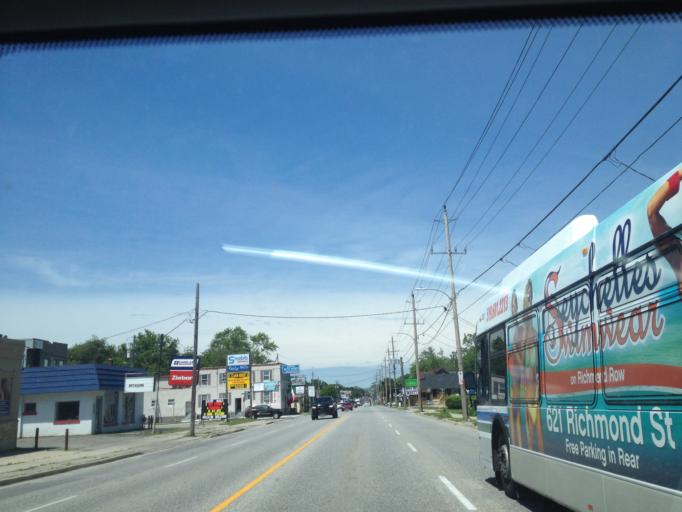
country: CA
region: Ontario
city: London
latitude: 42.9653
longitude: -81.2614
